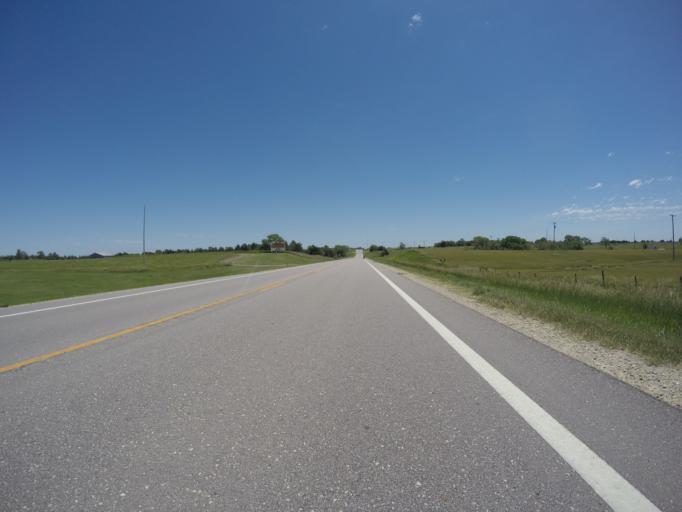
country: US
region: Kansas
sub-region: Republic County
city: Belleville
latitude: 39.8128
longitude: -97.6582
